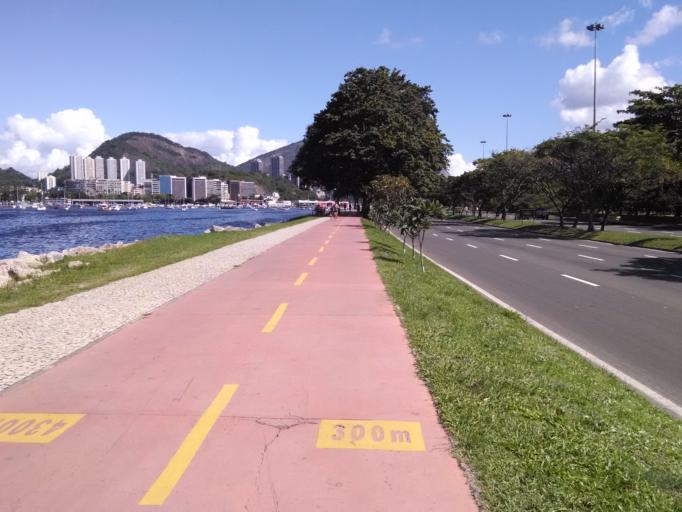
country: BR
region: Rio de Janeiro
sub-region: Rio De Janeiro
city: Rio de Janeiro
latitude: -22.9419
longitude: -43.1712
